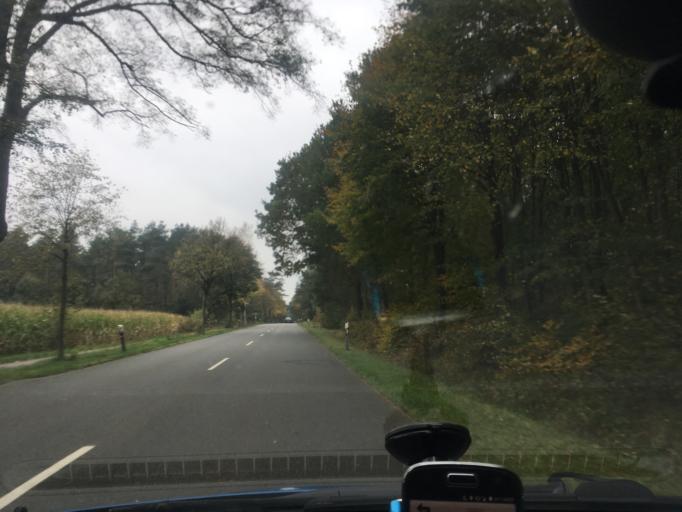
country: DE
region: Lower Saxony
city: Soderstorf
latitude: 53.1234
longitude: 10.1011
